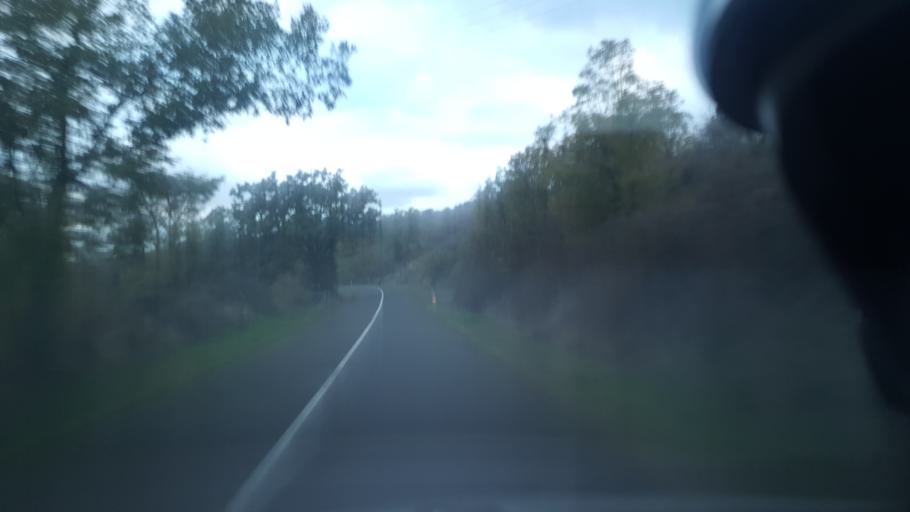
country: ES
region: Castille and Leon
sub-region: Provincia de Segovia
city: Vegas de Matute
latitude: 40.7267
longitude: -4.2869
